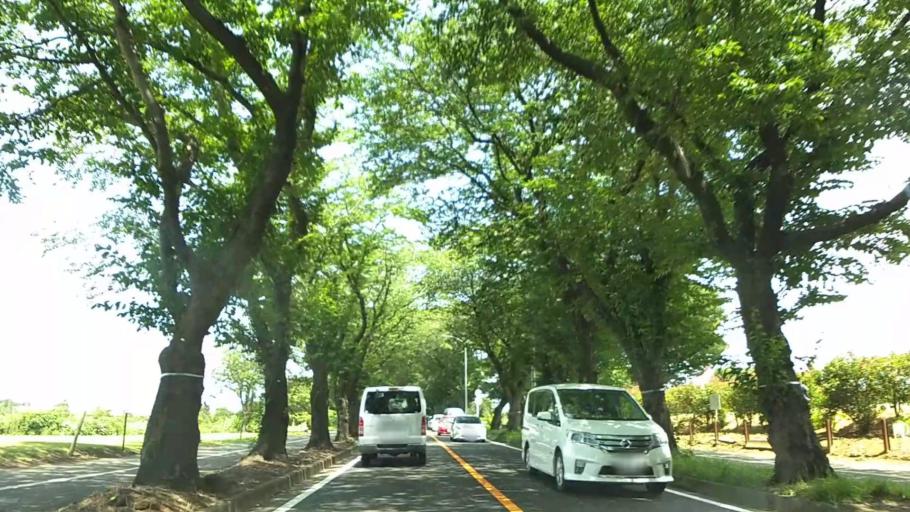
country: JP
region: Kanagawa
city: Minami-rinkan
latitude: 35.4856
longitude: 139.4804
